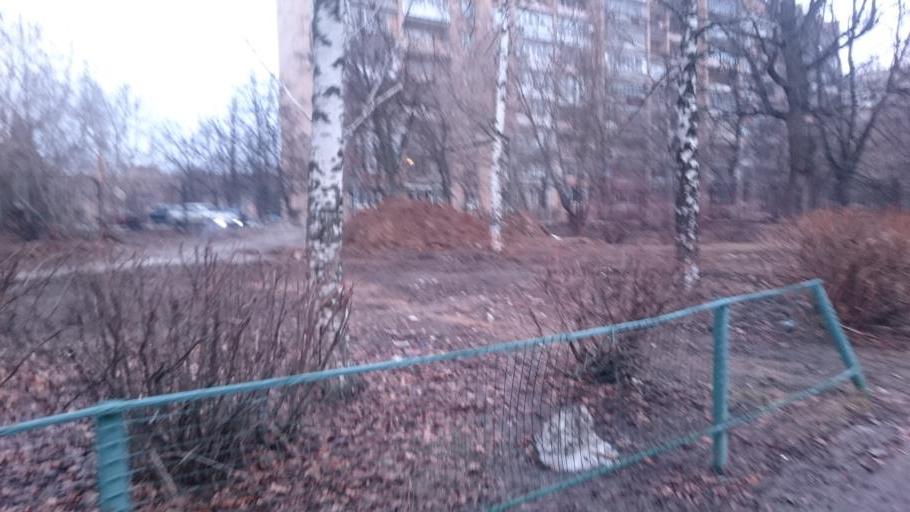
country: RU
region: Moskovskaya
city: Novoivanovskoye
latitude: 55.7037
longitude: 37.3611
